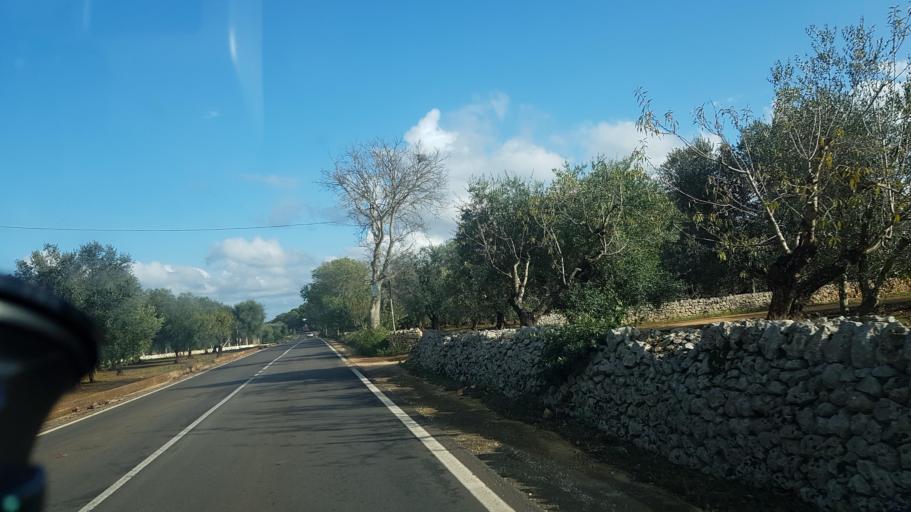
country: IT
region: Apulia
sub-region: Provincia di Brindisi
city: San Michele Salentino
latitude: 40.6464
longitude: 17.6145
